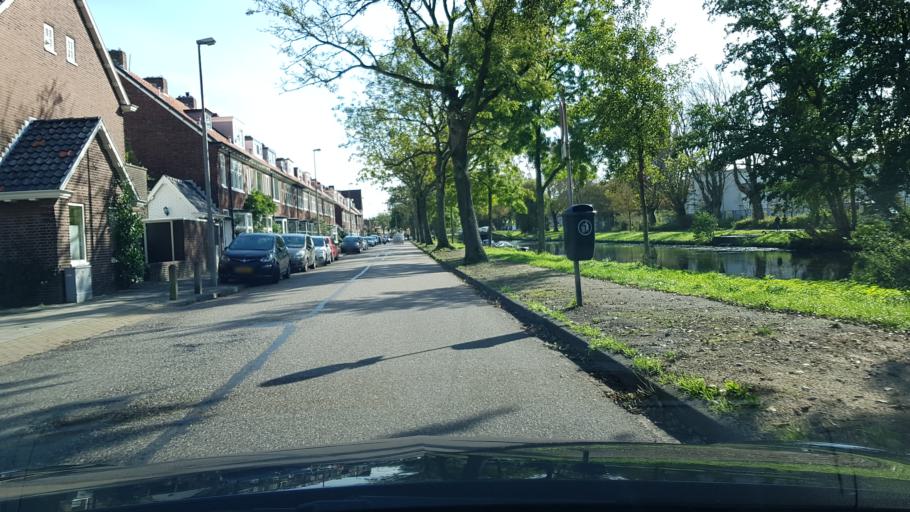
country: NL
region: North Holland
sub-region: Gemeente Bloemendaal
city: Bloemendaal
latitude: 52.4115
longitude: 4.6491
